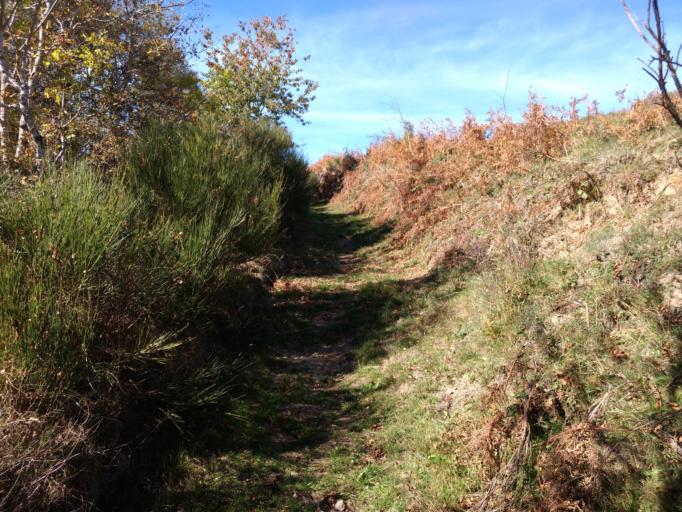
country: FR
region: Auvergne
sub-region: Departement du Cantal
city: Chaudes-Aigues
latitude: 44.8612
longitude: 2.9999
